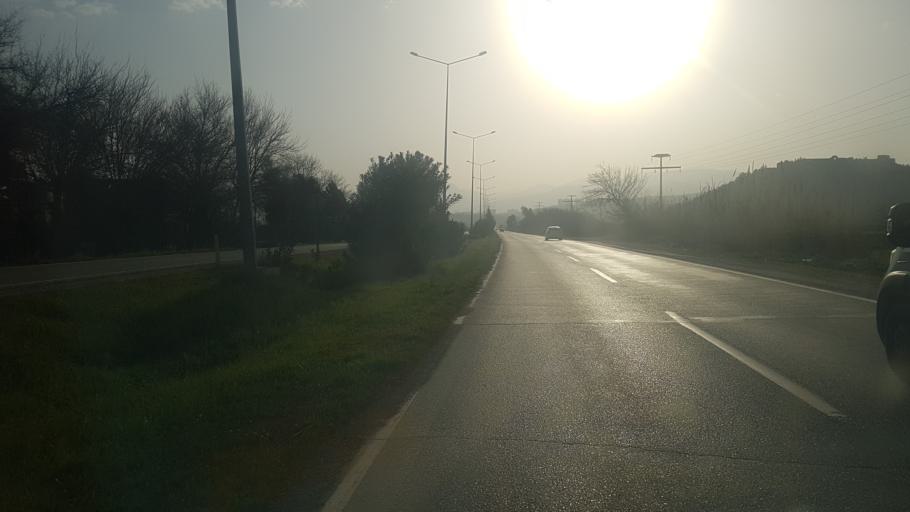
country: TR
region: Osmaniye
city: Toprakkale
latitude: 37.0559
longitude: 36.1260
